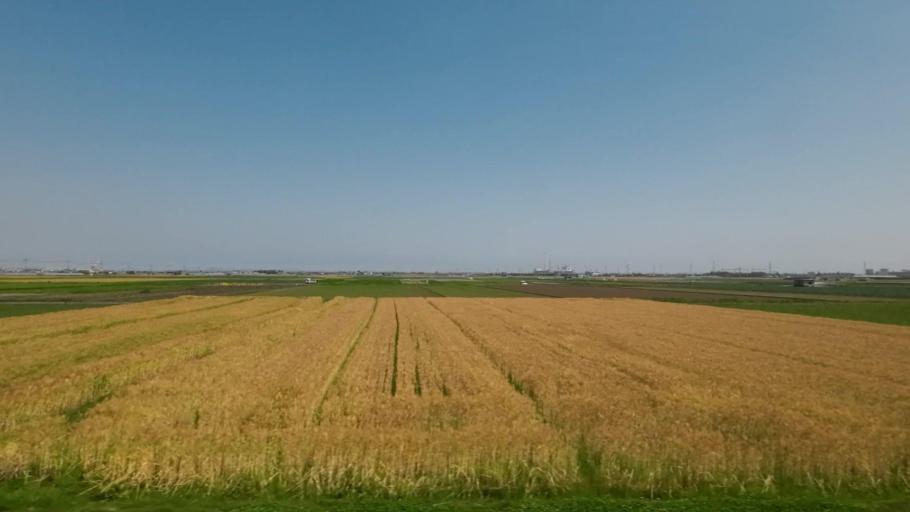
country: JP
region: Ehime
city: Saijo
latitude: 33.8959
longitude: 133.1597
